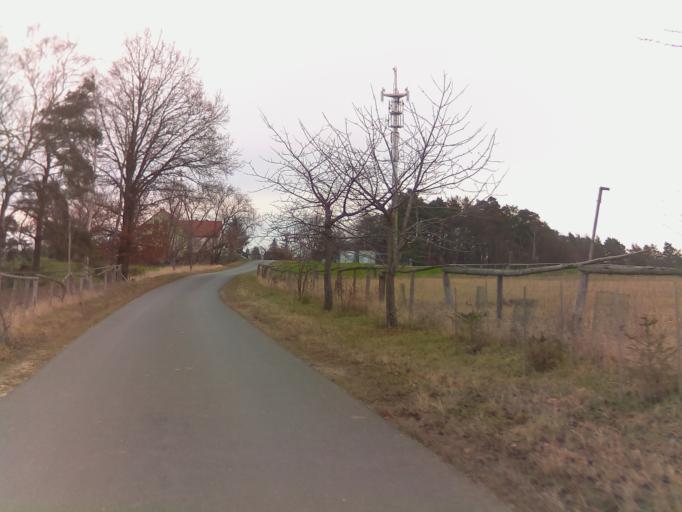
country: DE
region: Thuringia
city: Saara
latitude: 50.8641
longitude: 11.9612
